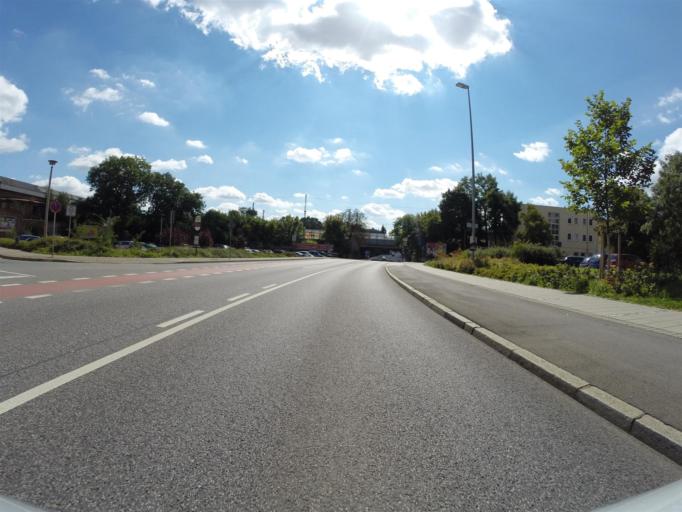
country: DE
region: Thuringia
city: Erfurt
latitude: 50.9712
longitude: 11.0307
